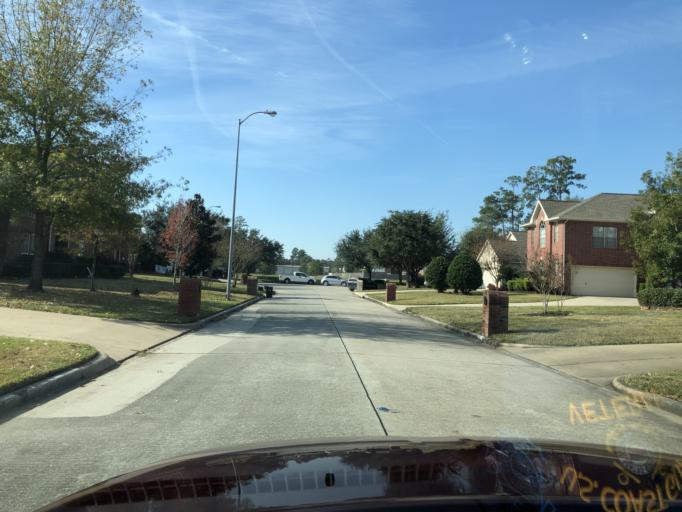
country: US
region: Texas
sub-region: Harris County
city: Tomball
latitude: 30.0252
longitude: -95.5581
